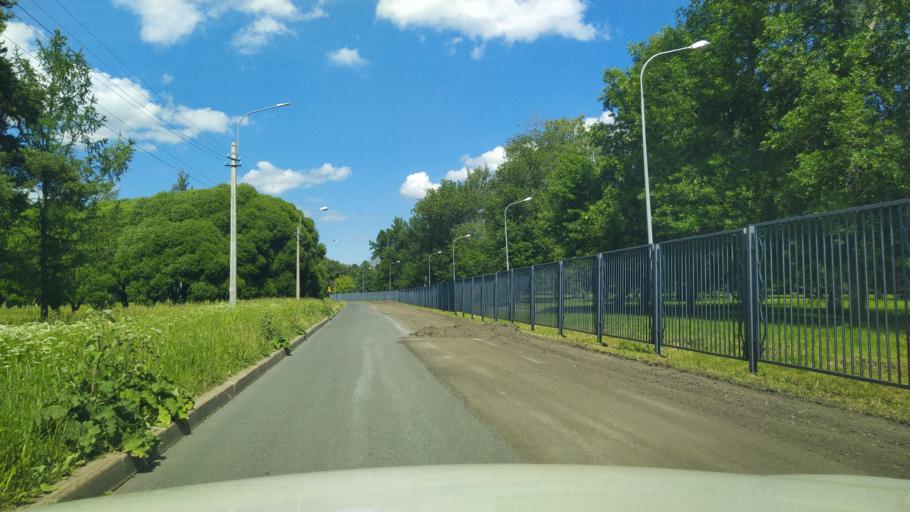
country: RU
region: Leningrad
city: Kalininskiy
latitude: 59.9981
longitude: 30.4173
